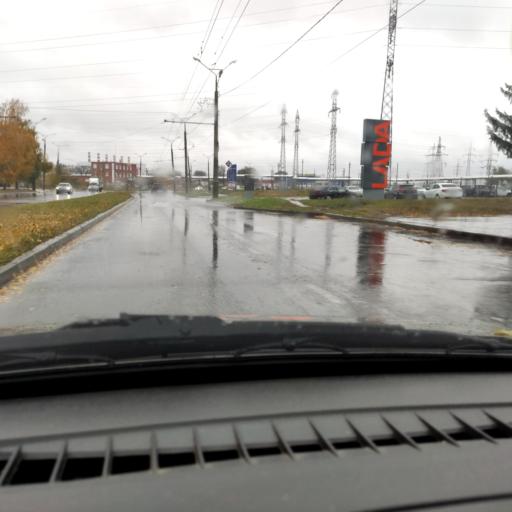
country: RU
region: Samara
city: Tol'yatti
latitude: 53.5331
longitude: 49.4345
